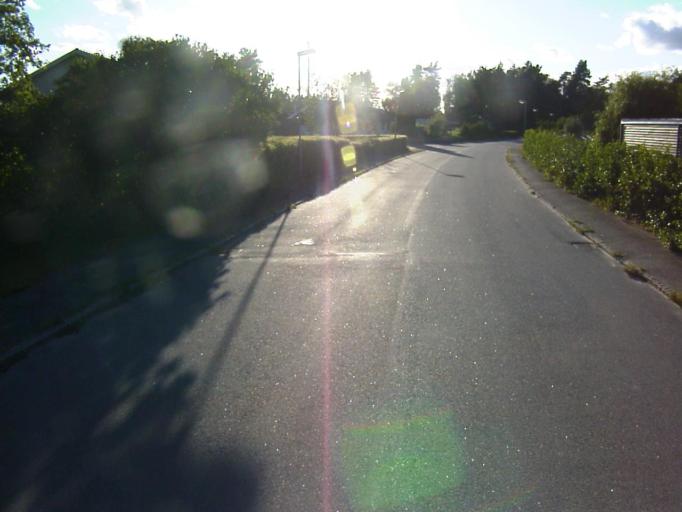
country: SE
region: Soedermanland
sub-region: Eskilstuna Kommun
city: Eskilstuna
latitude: 59.3907
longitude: 16.5139
